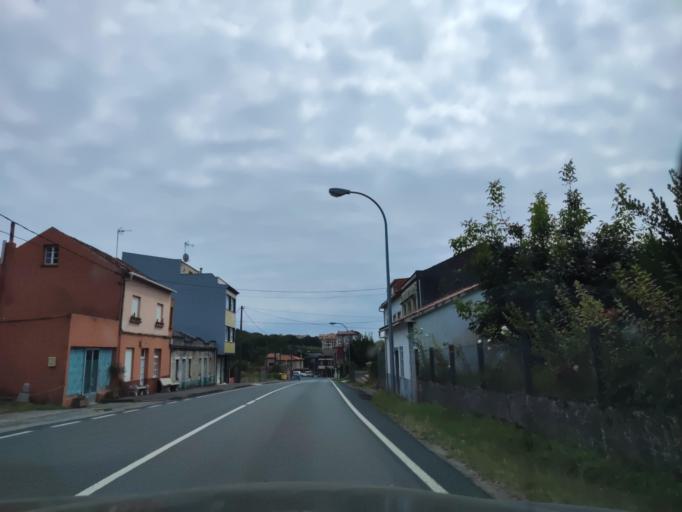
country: ES
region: Galicia
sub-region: Provincia da Coruna
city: Boiro
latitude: 42.6466
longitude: -8.8955
